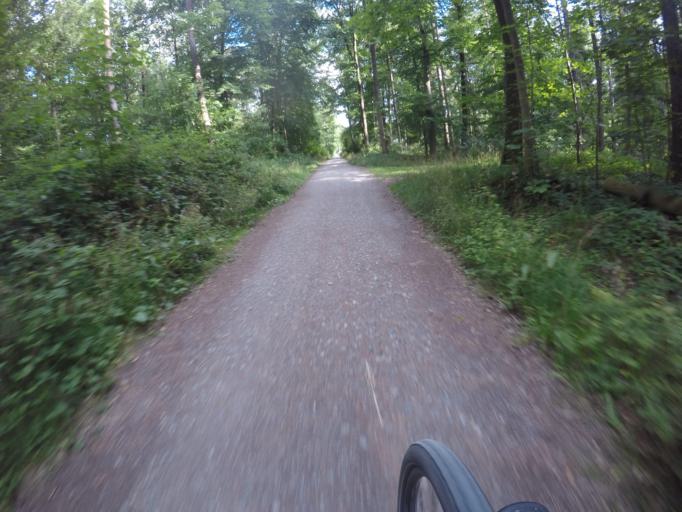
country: DE
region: Baden-Wuerttemberg
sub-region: Regierungsbezirk Stuttgart
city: Stuttgart-Ost
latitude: 48.7491
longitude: 9.2012
